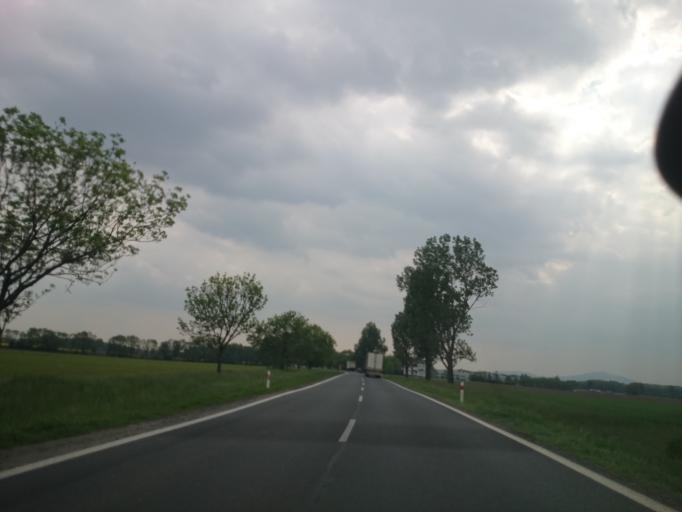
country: PL
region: Lower Silesian Voivodeship
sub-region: Powiat wroclawski
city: Kobierzyce
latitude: 50.9598
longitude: 16.9184
